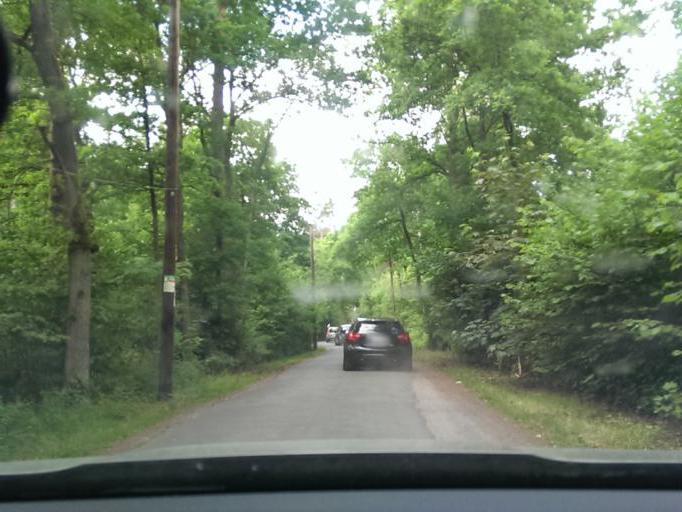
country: DE
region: Lower Saxony
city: Langenhagen
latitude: 52.5003
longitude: 9.7728
